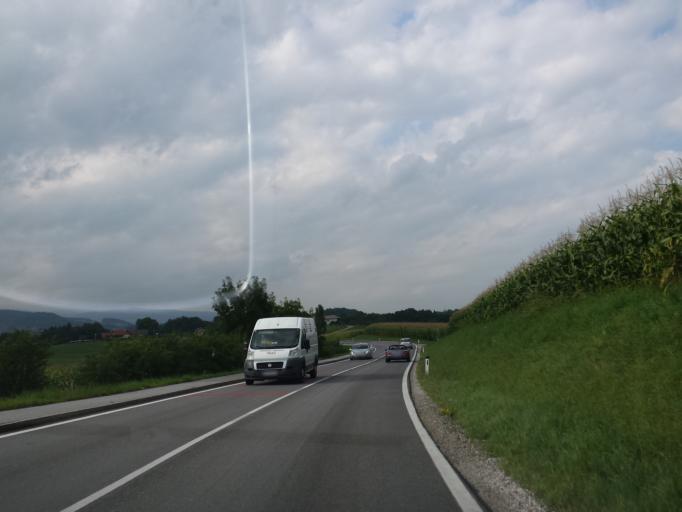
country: AT
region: Styria
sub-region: Politischer Bezirk Deutschlandsberg
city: Rassach
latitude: 46.8616
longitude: 15.2663
